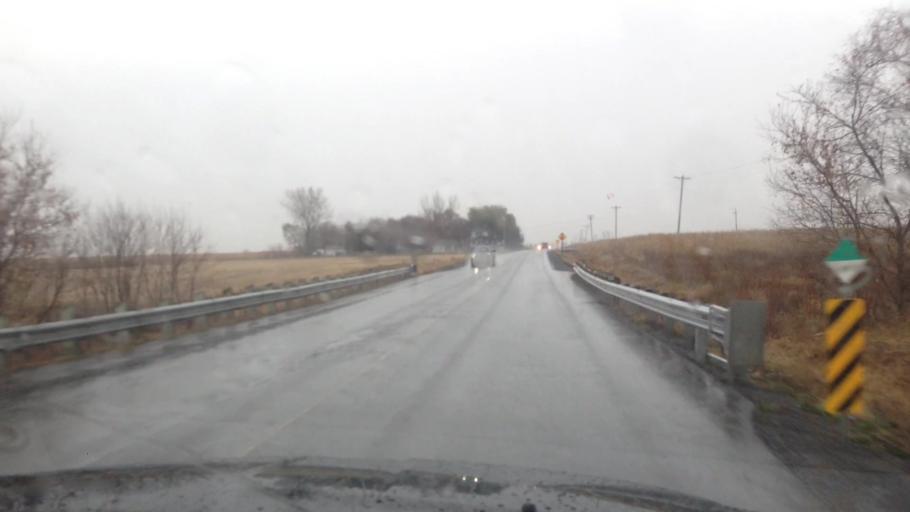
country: CA
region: Ontario
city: Bourget
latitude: 45.2859
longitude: -75.2855
